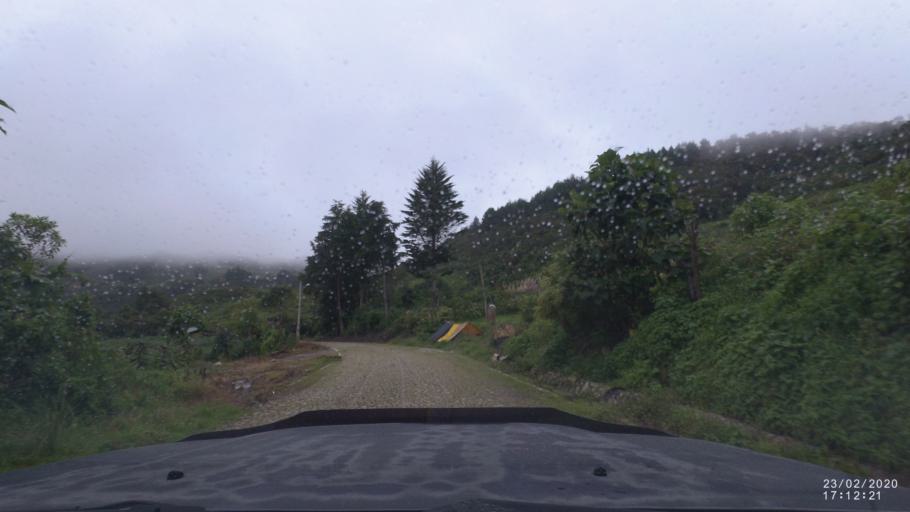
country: BO
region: Cochabamba
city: Colomi
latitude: -17.1342
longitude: -65.9432
